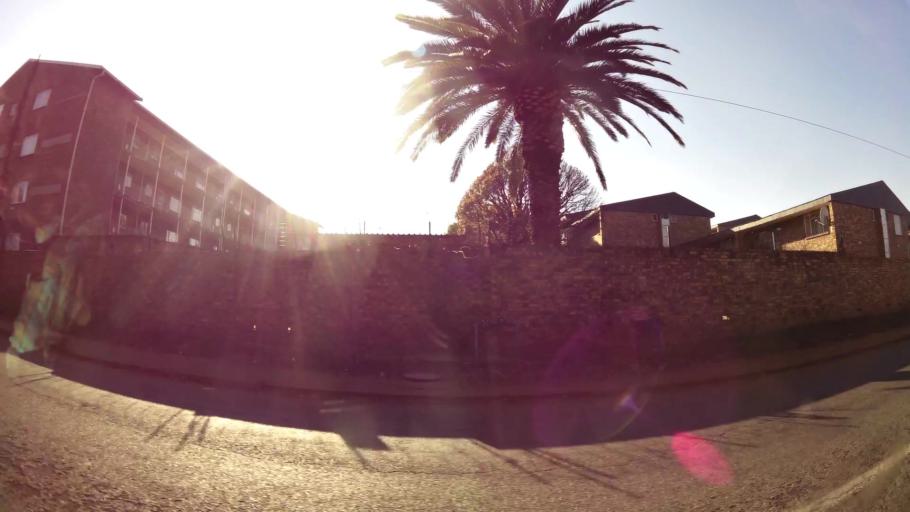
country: ZA
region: Gauteng
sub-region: City of Johannesburg Metropolitan Municipality
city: Modderfontein
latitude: -26.1395
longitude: 28.1651
